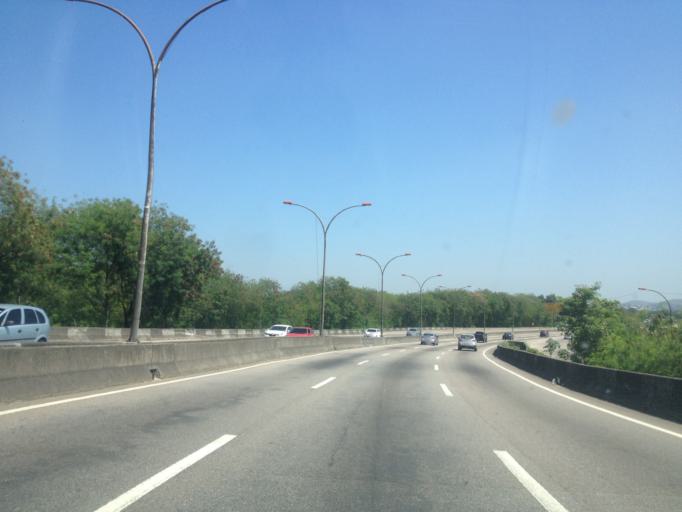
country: BR
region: Rio de Janeiro
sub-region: Duque De Caxias
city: Duque de Caxias
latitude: -22.8078
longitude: -43.2915
